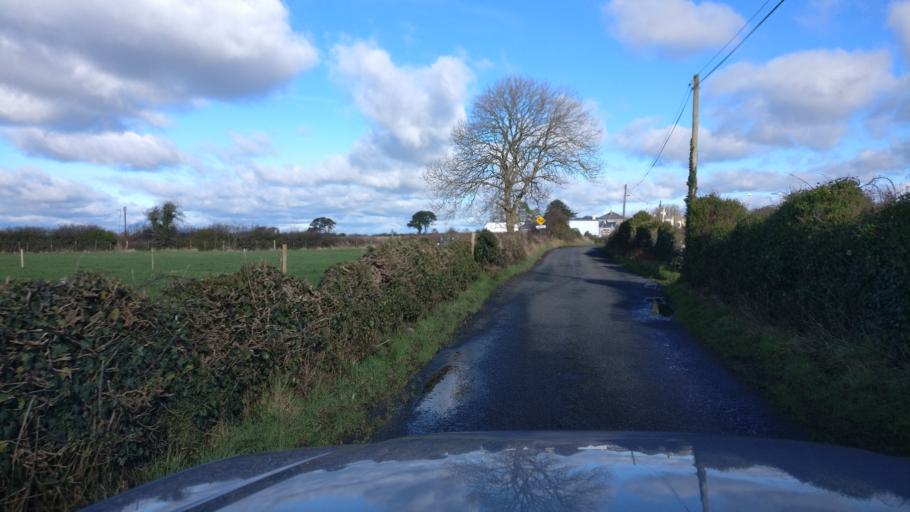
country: IE
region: Connaught
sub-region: County Galway
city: Oranmore
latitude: 53.2803
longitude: -8.9022
